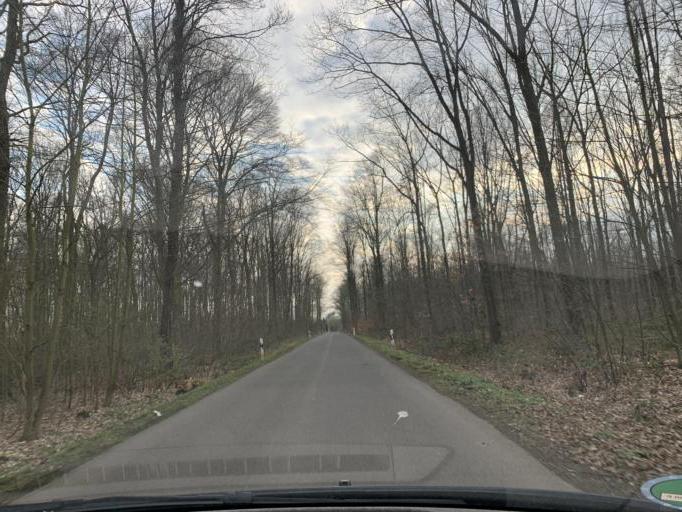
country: DE
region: North Rhine-Westphalia
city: Julich
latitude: 50.9314
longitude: 6.4078
